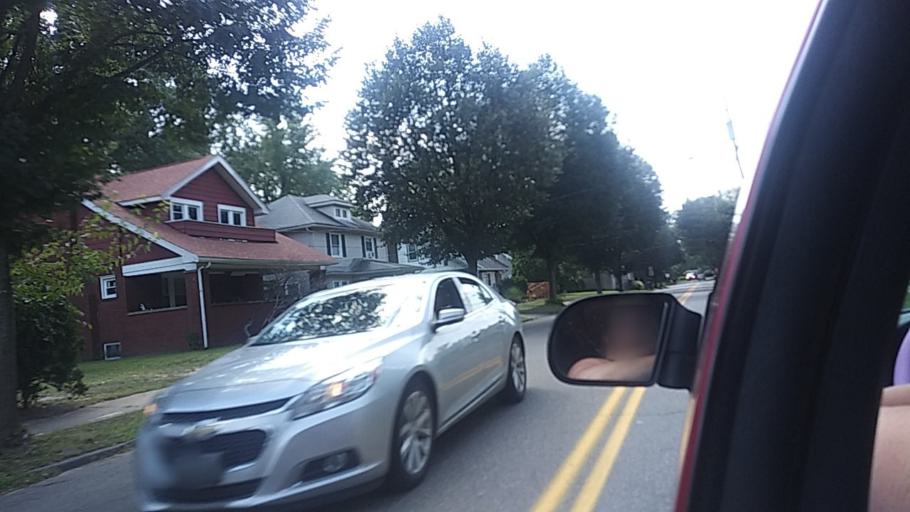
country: US
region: Ohio
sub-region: Summit County
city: Akron
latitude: 41.0924
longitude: -81.5543
